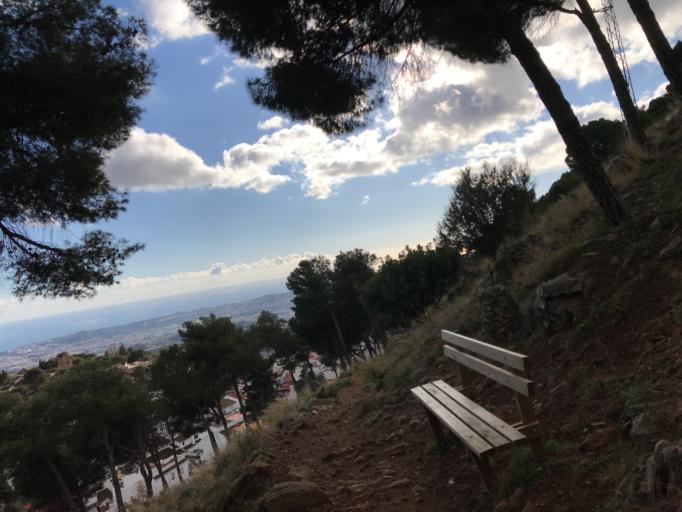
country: ES
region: Andalusia
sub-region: Provincia de Malaga
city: Mijas
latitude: 36.5972
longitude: -4.6391
